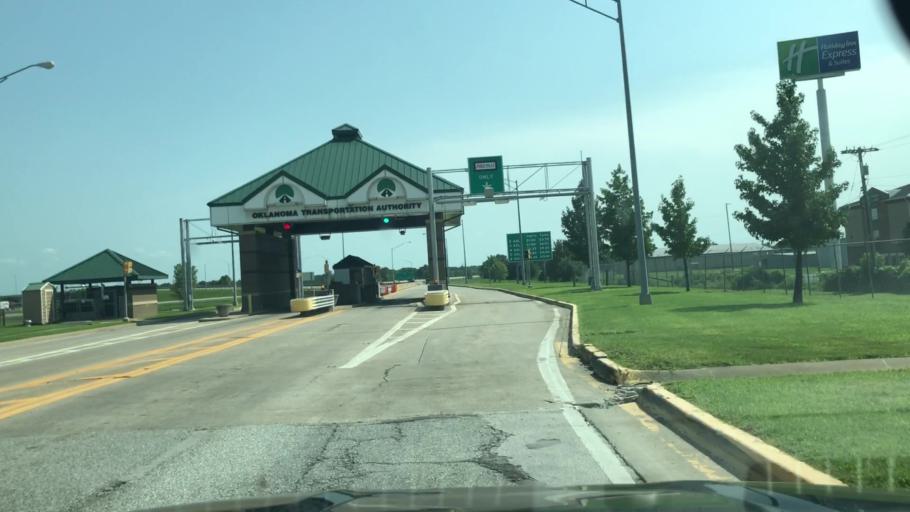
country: US
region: Oklahoma
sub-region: Ottawa County
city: Miami
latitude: 36.8692
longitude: -94.8519
